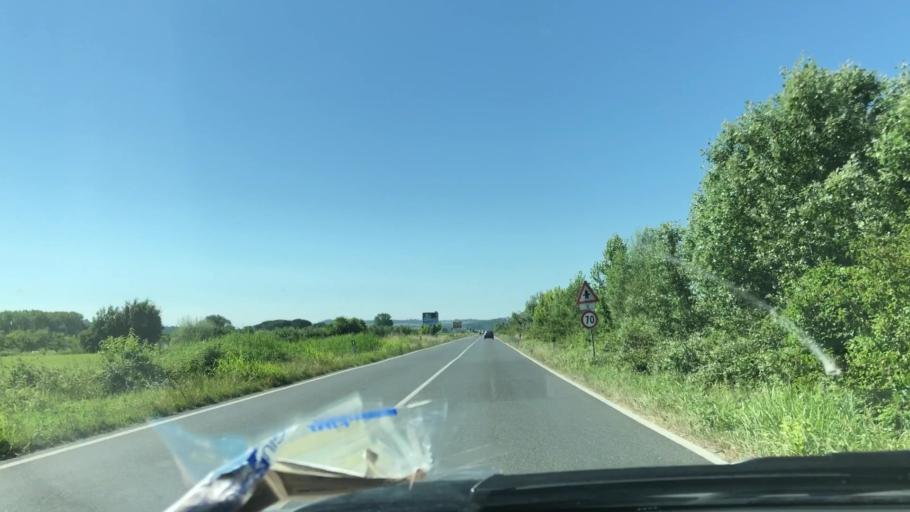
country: IT
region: Tuscany
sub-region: Province of Pisa
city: Forcoli
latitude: 43.5966
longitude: 10.6973
